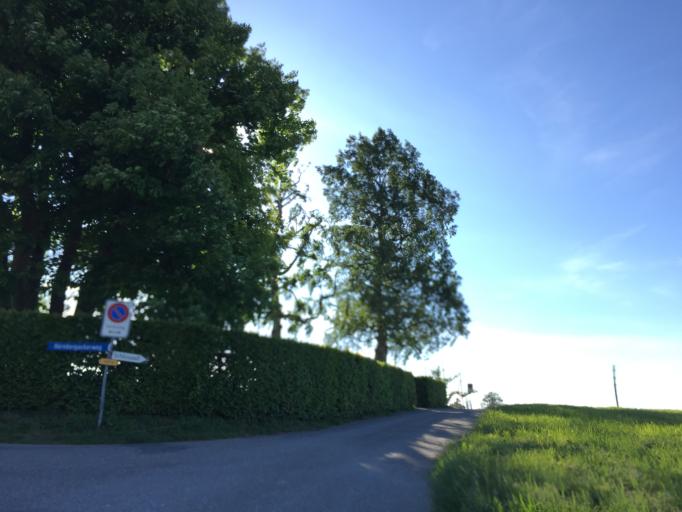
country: CH
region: Bern
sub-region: Bern-Mittelland District
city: Biglen
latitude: 46.9066
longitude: 7.6317
